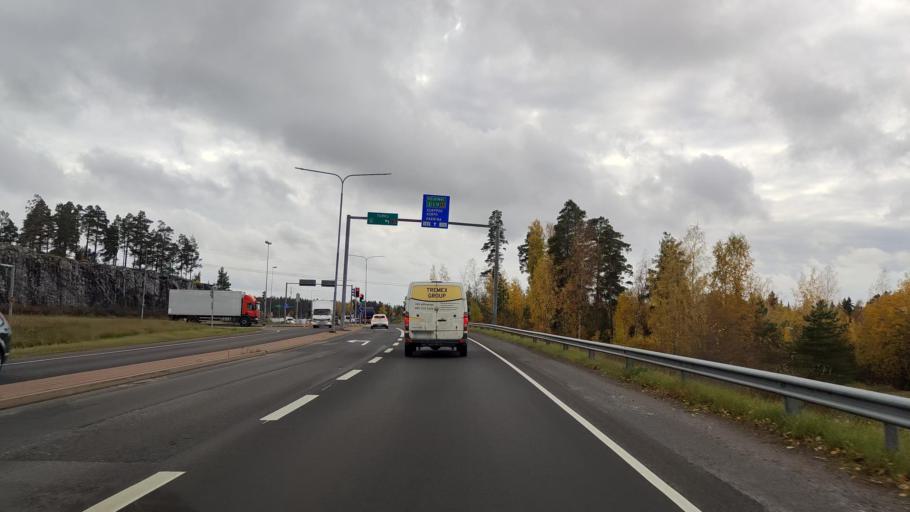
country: FI
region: Varsinais-Suomi
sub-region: Turku
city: Kaarina
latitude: 60.4261
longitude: 22.3805
